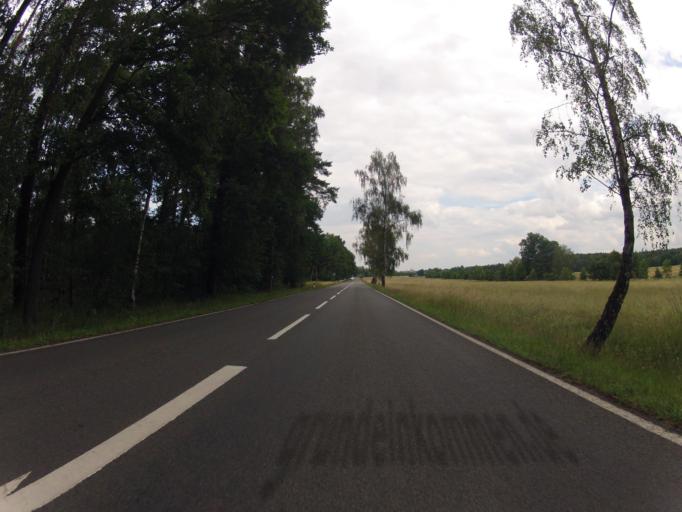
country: DE
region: Saxony
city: Schildau
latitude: 51.4317
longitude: 12.9248
